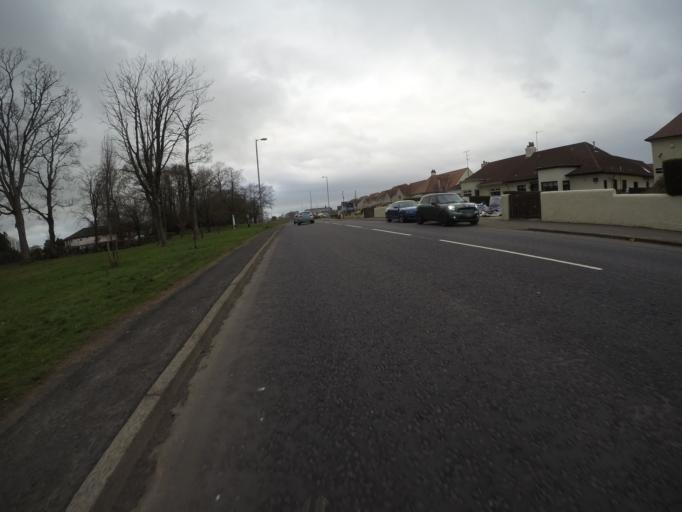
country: GB
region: Scotland
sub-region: East Ayrshire
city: Kilmarnock
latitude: 55.6114
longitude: -4.5223
